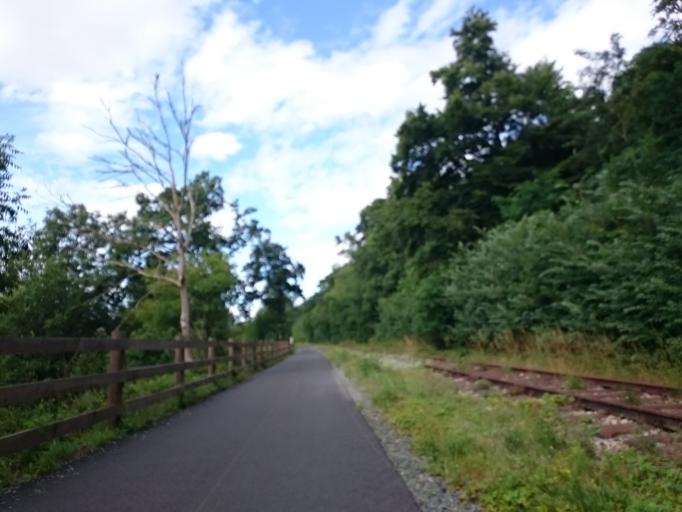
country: FR
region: Lower Normandy
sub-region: Departement du Calvados
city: Clinchamps-sur-Orne
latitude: 49.0715
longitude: -0.4322
